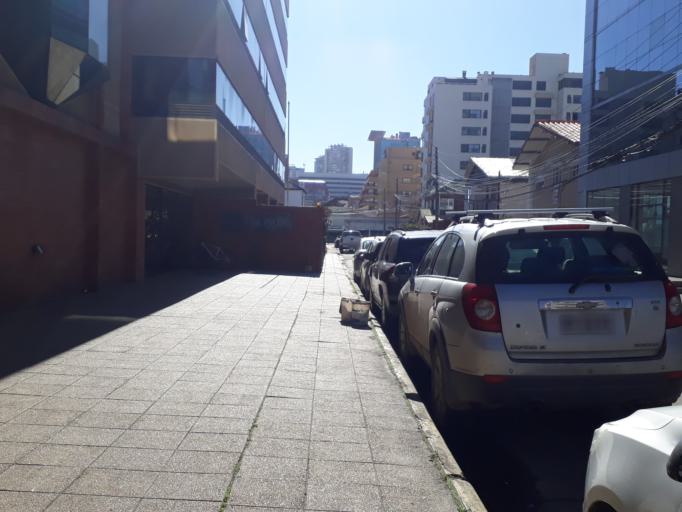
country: CL
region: Valparaiso
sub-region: Provincia de Valparaiso
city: Vina del Mar
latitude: -33.0140
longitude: -71.5485
